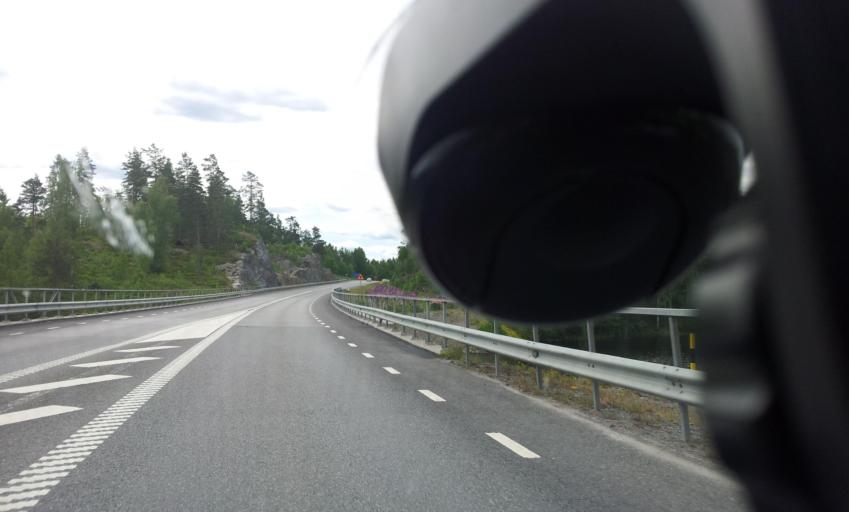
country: SE
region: Kalmar
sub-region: Vasterviks Kommun
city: Ankarsrum
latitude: 57.6614
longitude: 16.4445
